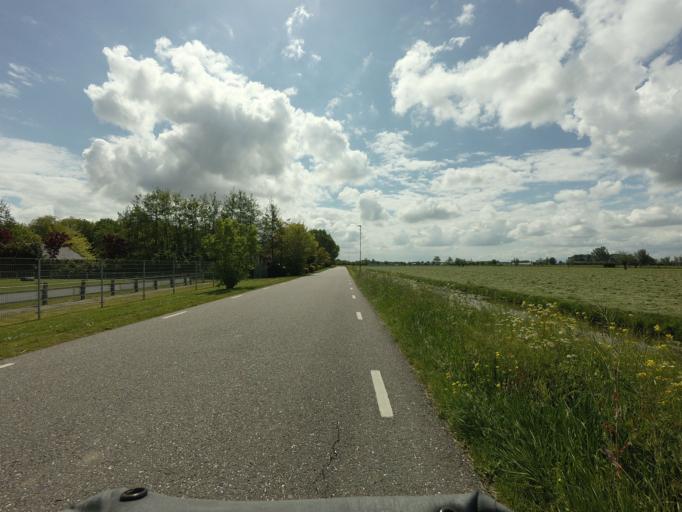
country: NL
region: South Holland
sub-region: Gemeente Gorinchem
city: Gorinchem
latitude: 51.8692
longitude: 4.9493
